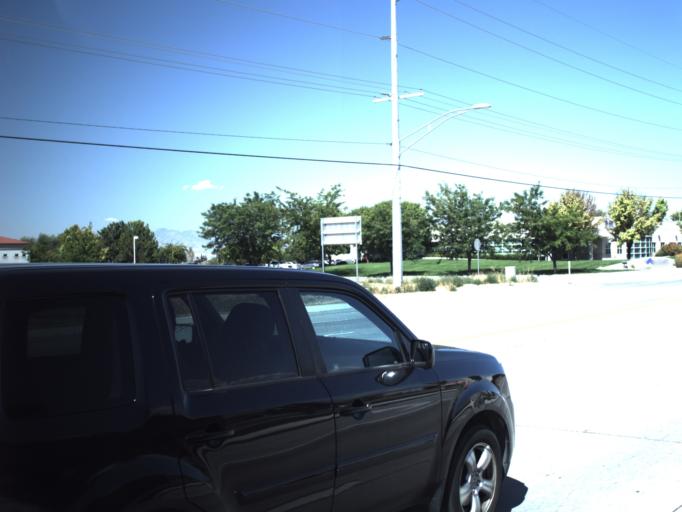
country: US
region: Utah
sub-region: Cache County
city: Logan
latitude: 41.7379
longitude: -111.8595
